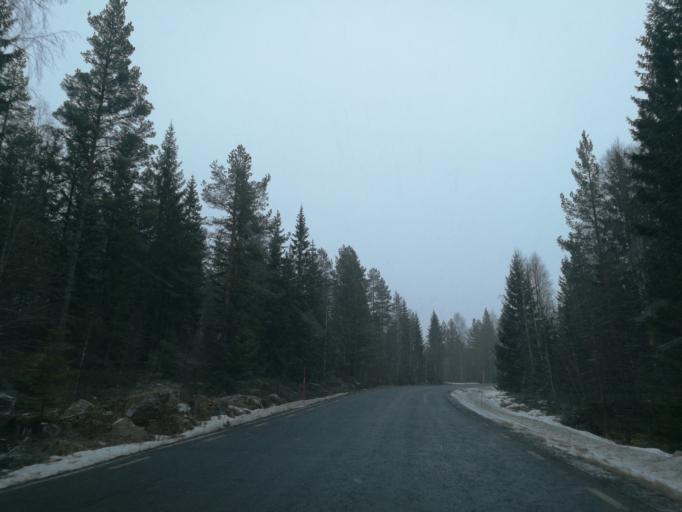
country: NO
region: Hedmark
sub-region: Grue
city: Kirkenaer
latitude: 60.6868
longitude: 12.6345
